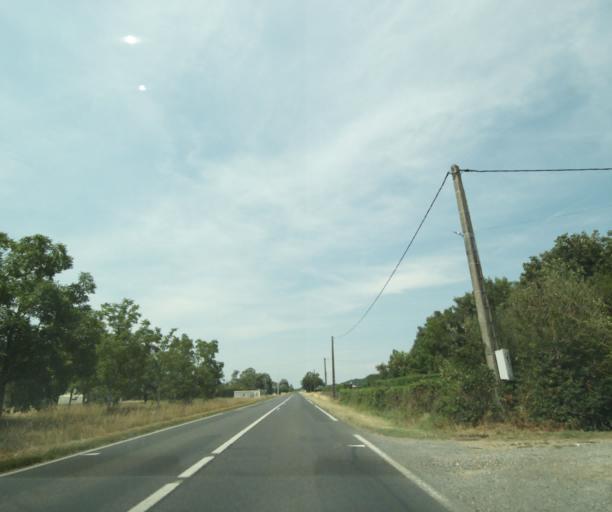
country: FR
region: Poitou-Charentes
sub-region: Departement de la Vienne
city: Bonneuil-Matours
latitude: 46.6498
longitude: 0.5861
